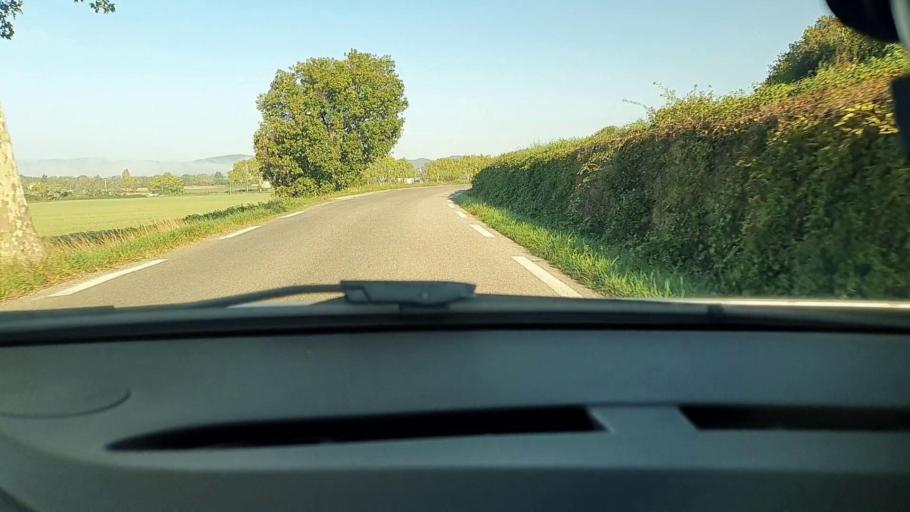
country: FR
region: Languedoc-Roussillon
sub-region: Departement du Gard
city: Barjac
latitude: 44.2476
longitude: 4.2936
